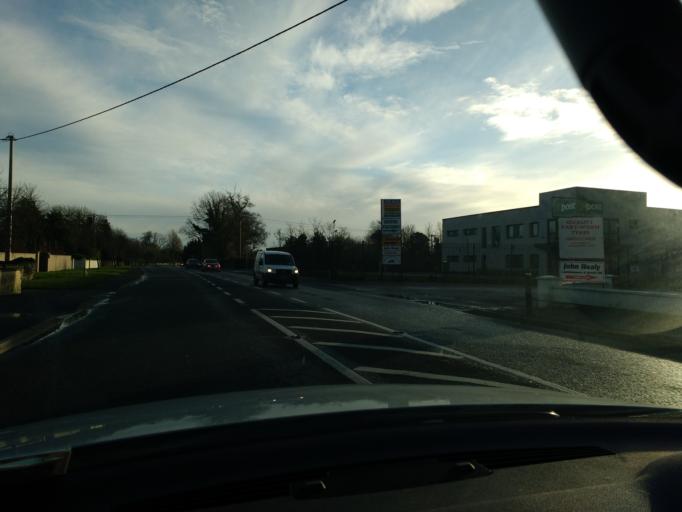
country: IE
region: Munster
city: Thurles
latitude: 52.6661
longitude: -7.8064
